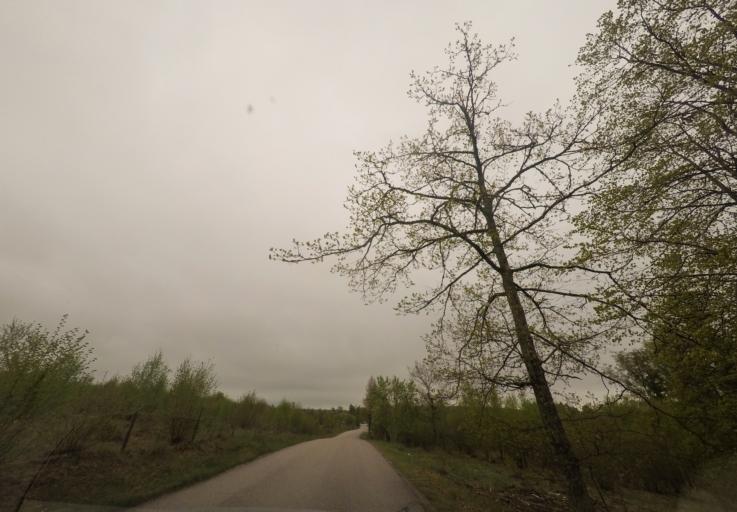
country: SE
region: Vaestmanland
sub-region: Vasteras
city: Vasteras
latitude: 59.5698
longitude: 16.6183
